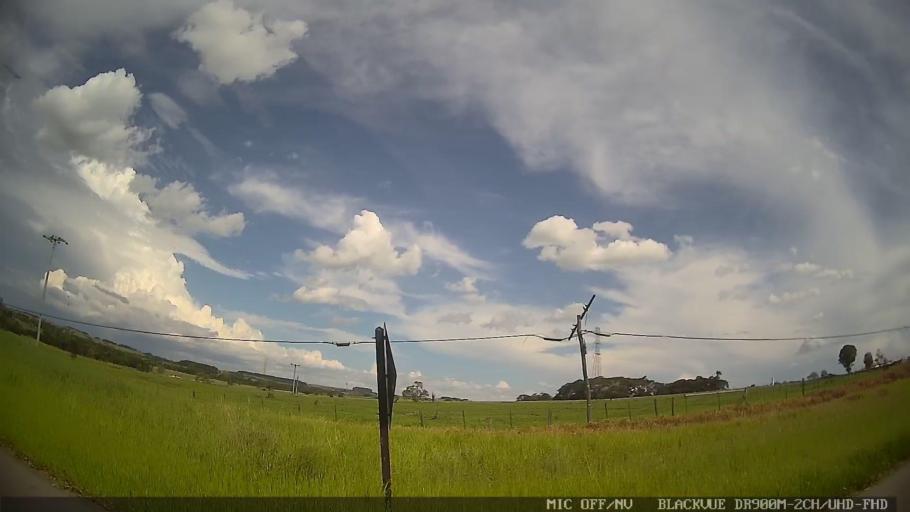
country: BR
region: Sao Paulo
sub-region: Conchas
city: Conchas
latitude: -23.0588
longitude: -47.9649
